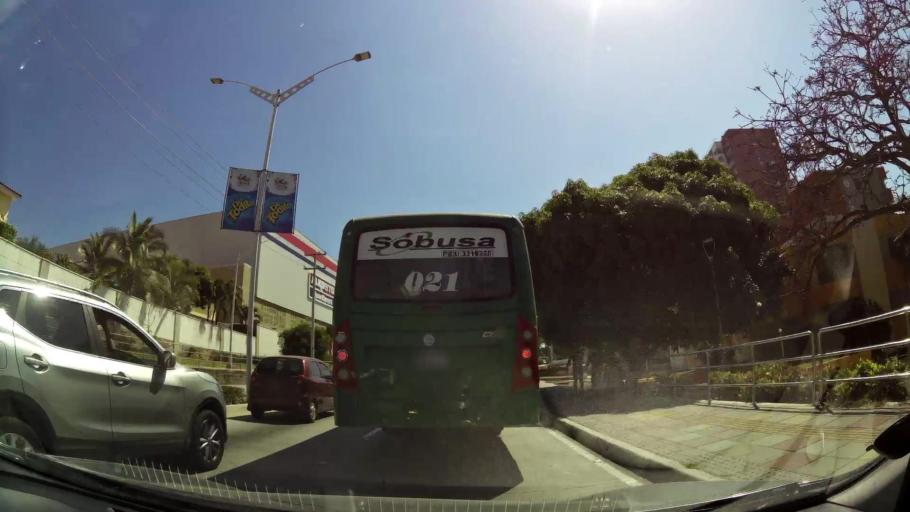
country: CO
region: Atlantico
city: Barranquilla
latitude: 11.0113
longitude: -74.8294
